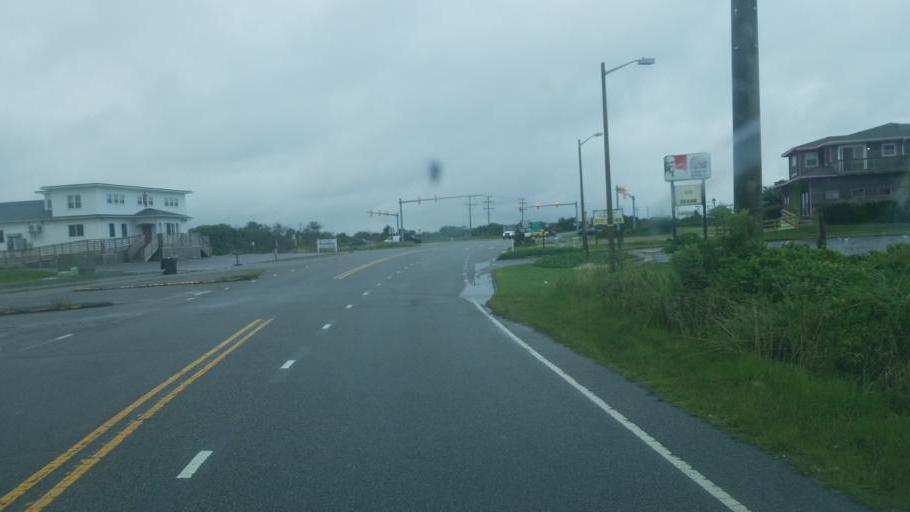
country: US
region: North Carolina
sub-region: Dare County
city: Nags Head
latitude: 35.9074
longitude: -75.5977
